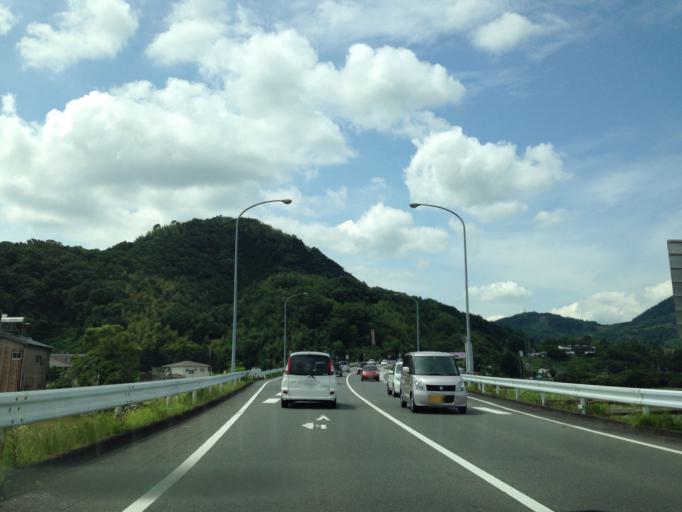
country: JP
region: Shizuoka
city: Mishima
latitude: 35.0546
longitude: 138.9241
